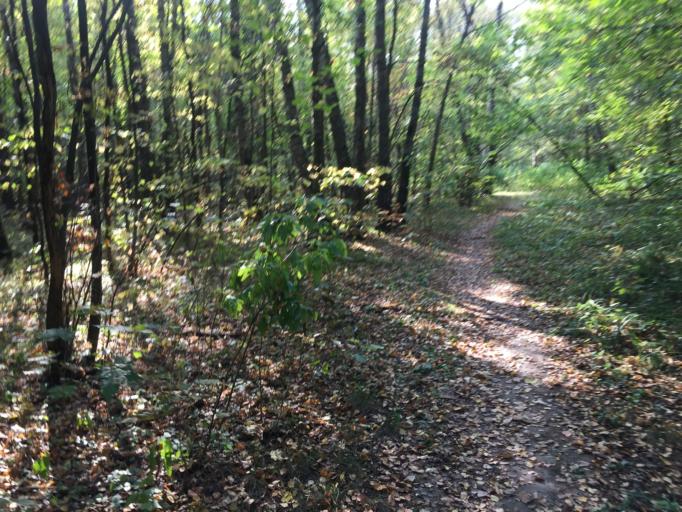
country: RU
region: Moscow
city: Babushkin
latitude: 55.8560
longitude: 37.7239
